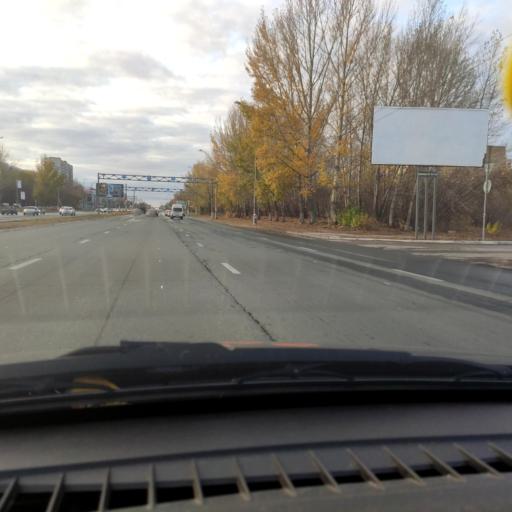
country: RU
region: Samara
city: Tol'yatti
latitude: 53.5395
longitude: 49.2841
